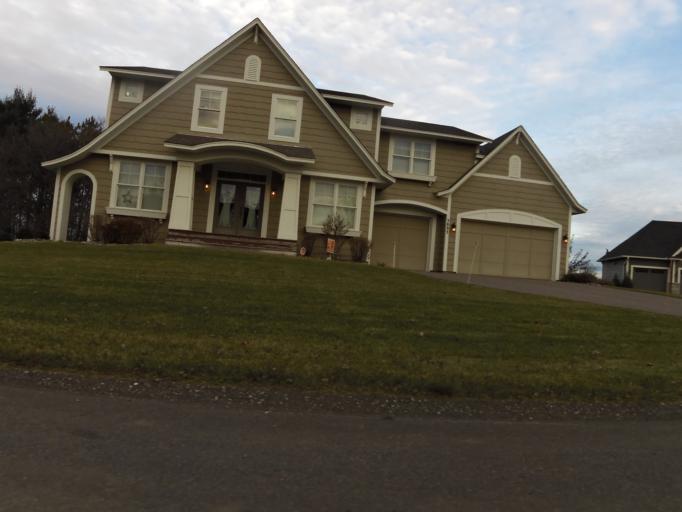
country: US
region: Minnesota
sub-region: Washington County
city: Bayport
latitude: 45.0043
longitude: -92.7969
